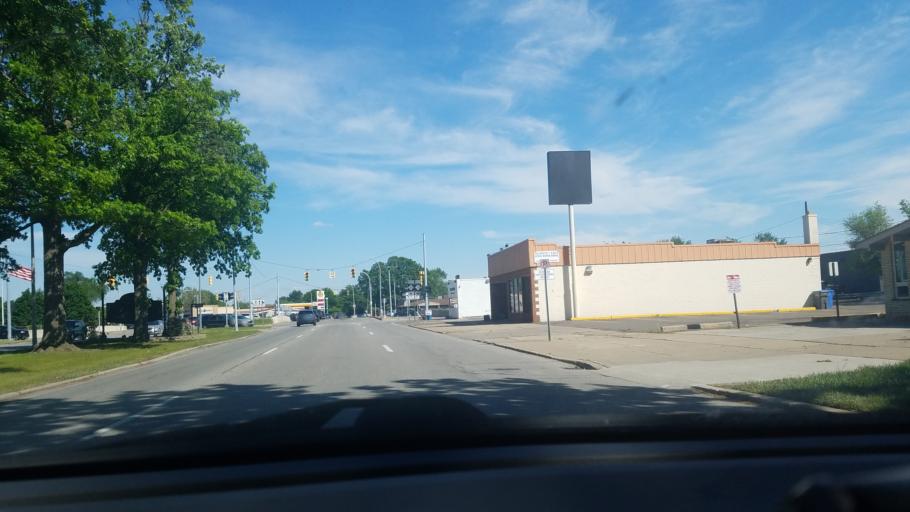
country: US
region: Michigan
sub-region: Wayne County
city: Allen Park
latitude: 42.2782
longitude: -83.2185
